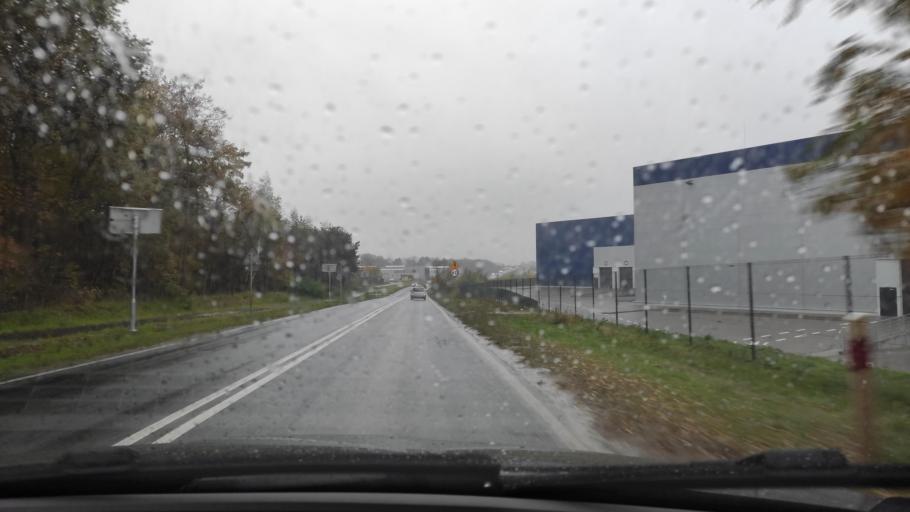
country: PL
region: Greater Poland Voivodeship
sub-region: Powiat poznanski
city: Daszewice
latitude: 52.3257
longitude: 17.0420
